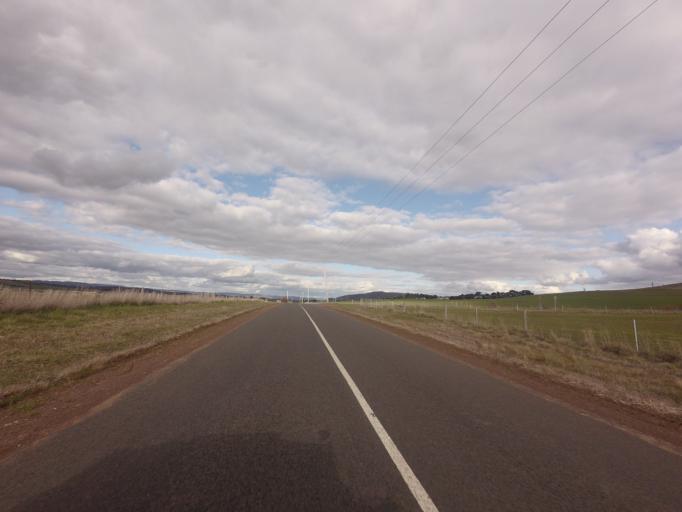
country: AU
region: Tasmania
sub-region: Northern Midlands
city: Evandale
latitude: -41.8915
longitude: 147.3319
